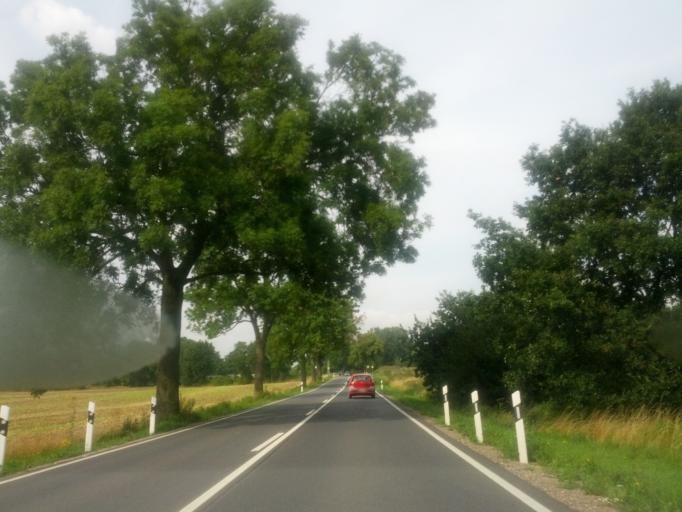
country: DE
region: Mecklenburg-Vorpommern
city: Sellin
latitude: 53.9346
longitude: 11.6061
